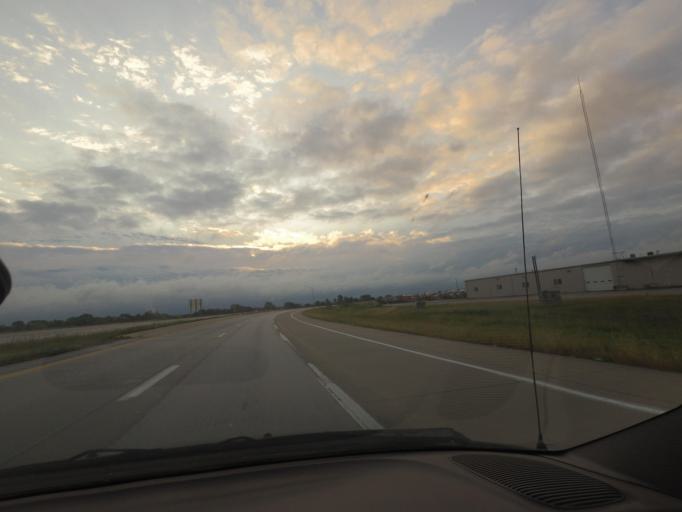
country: US
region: Missouri
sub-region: Shelby County
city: Shelbina
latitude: 39.6978
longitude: -92.0340
